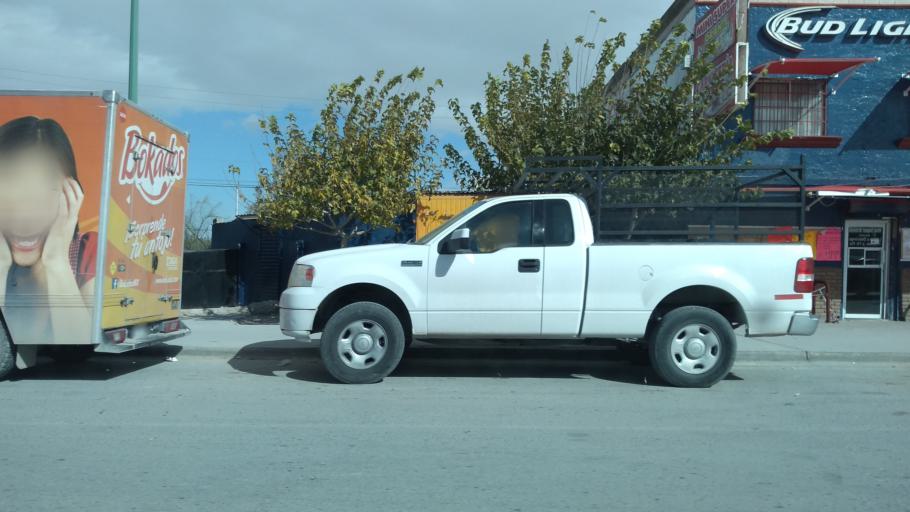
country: US
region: Texas
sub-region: El Paso County
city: San Elizario
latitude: 31.5659
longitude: -106.3392
